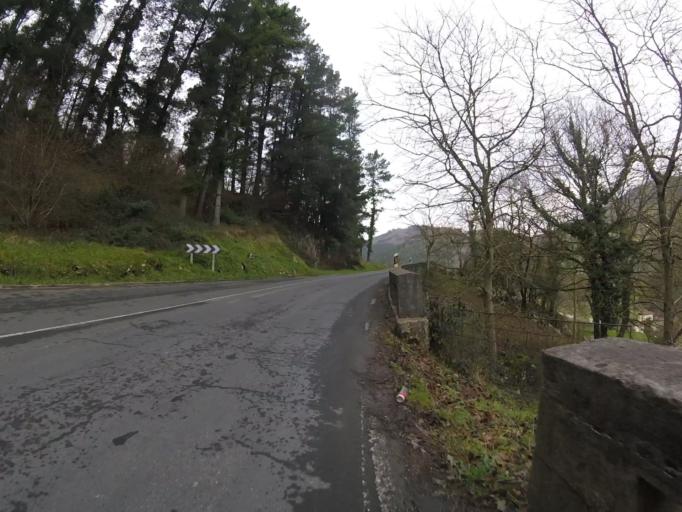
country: ES
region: Basque Country
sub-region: Provincia de Guipuzcoa
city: Albiztur
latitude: 43.1270
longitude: -2.1322
